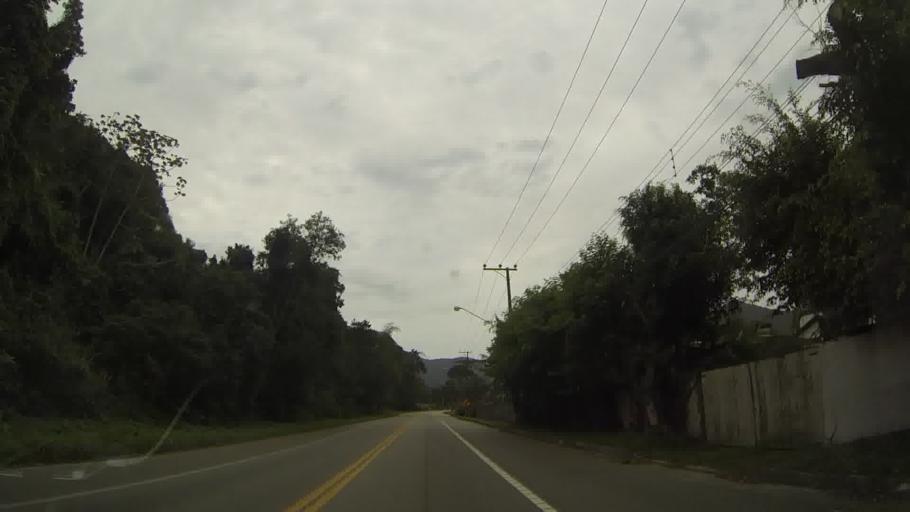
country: BR
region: Sao Paulo
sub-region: Sao Sebastiao
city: Sao Sebastiao
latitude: -23.8173
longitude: -45.4623
